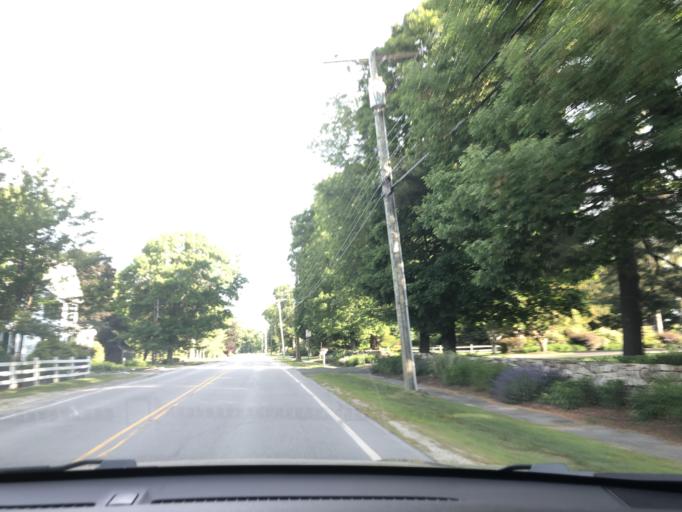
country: US
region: New Hampshire
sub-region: Merrimack County
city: New London
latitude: 43.4084
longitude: -71.9734
